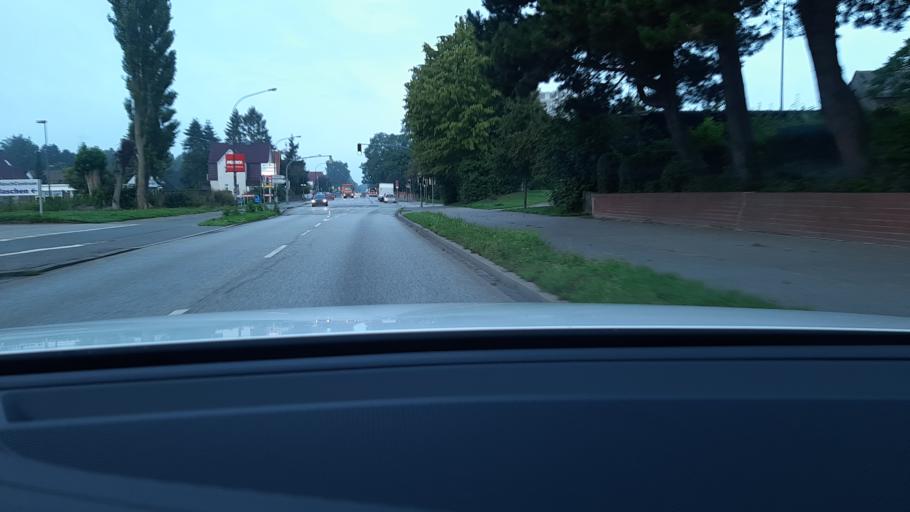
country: DE
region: Schleswig-Holstein
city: Stockelsdorf
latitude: 53.8629
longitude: 10.6520
